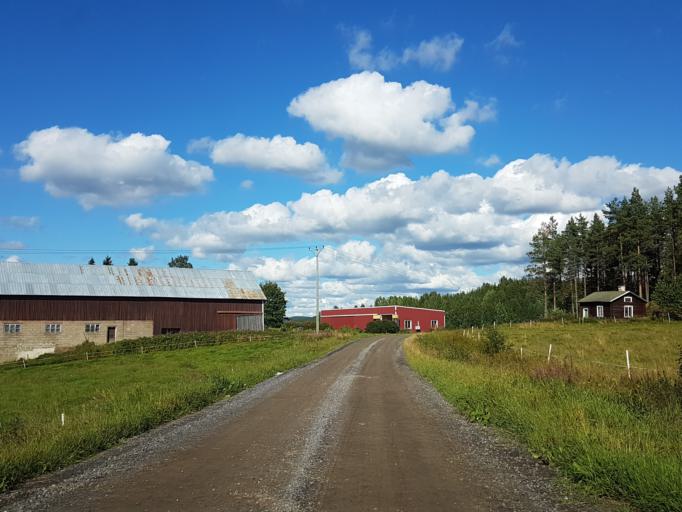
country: SE
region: Vaesterbotten
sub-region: Skelleftea Kommun
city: Burtraesk
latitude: 64.2971
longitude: 20.4863
